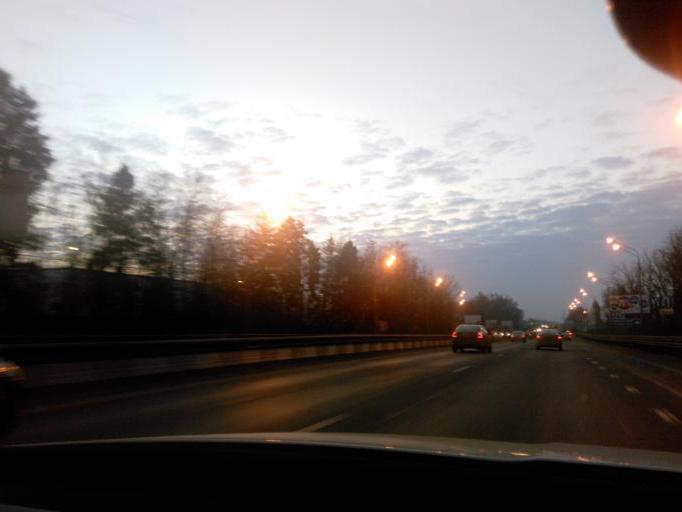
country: RU
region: Moskovskaya
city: Skhodnya
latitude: 55.9827
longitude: 37.2881
